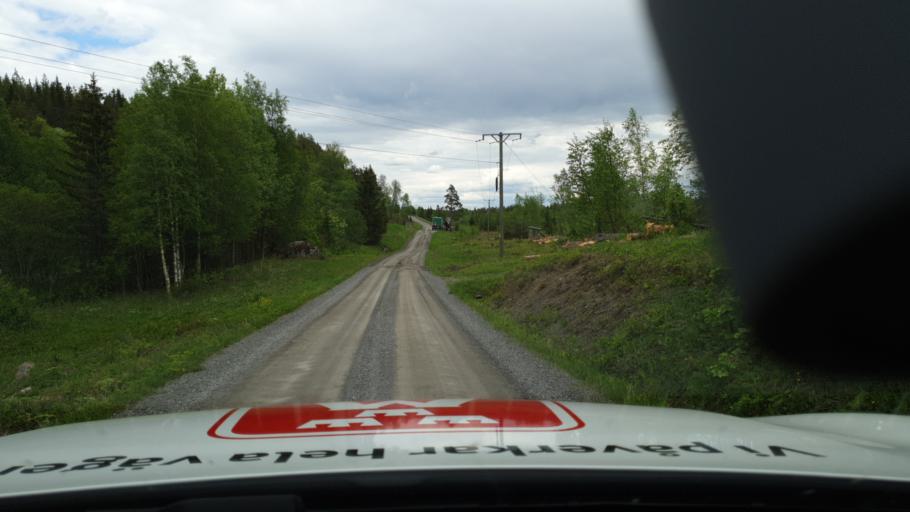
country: SE
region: Jaemtland
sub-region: OEstersunds Kommun
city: Brunflo
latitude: 62.9688
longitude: 14.6933
